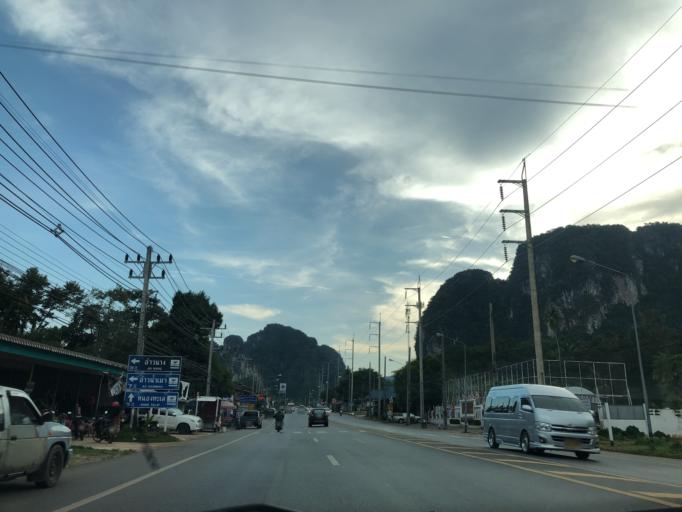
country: TH
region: Krabi
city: Krabi
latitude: 8.0818
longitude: 98.8599
